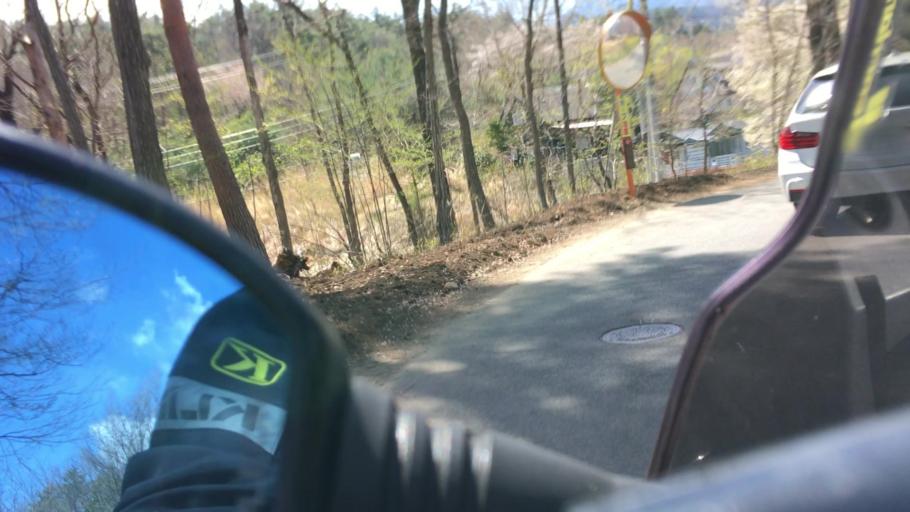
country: JP
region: Yamanashi
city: Nirasaki
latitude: 35.7777
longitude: 138.3474
